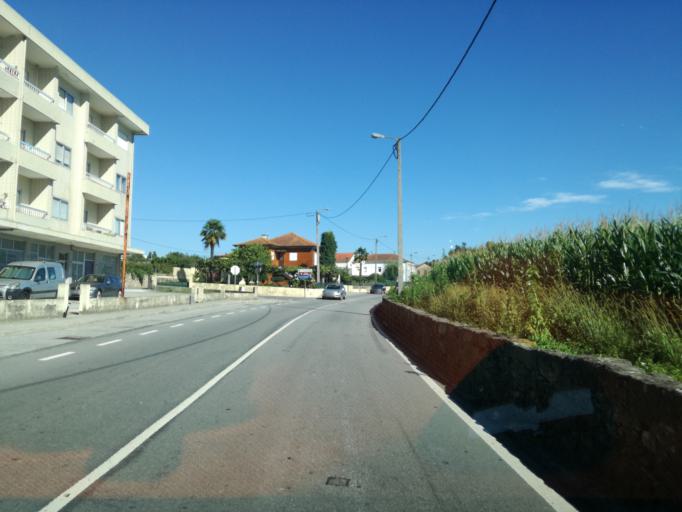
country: PT
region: Porto
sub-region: Trofa
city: Sao Romao do Coronado
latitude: 41.2831
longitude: -8.5647
